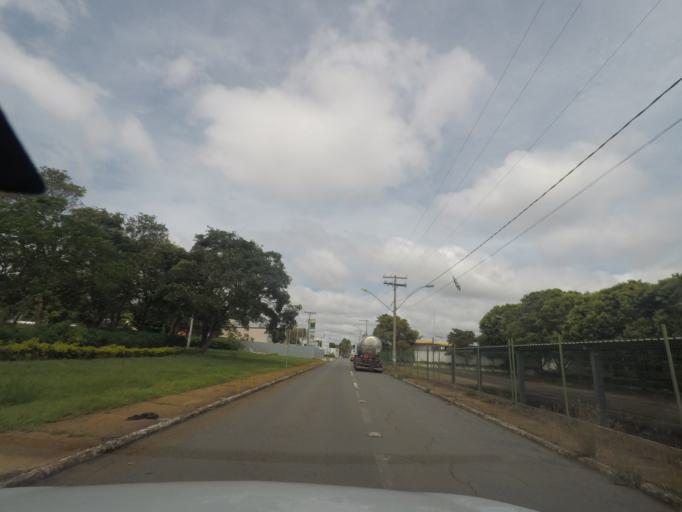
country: BR
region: Goias
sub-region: Goiania
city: Goiania
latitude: -16.6324
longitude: -49.2273
